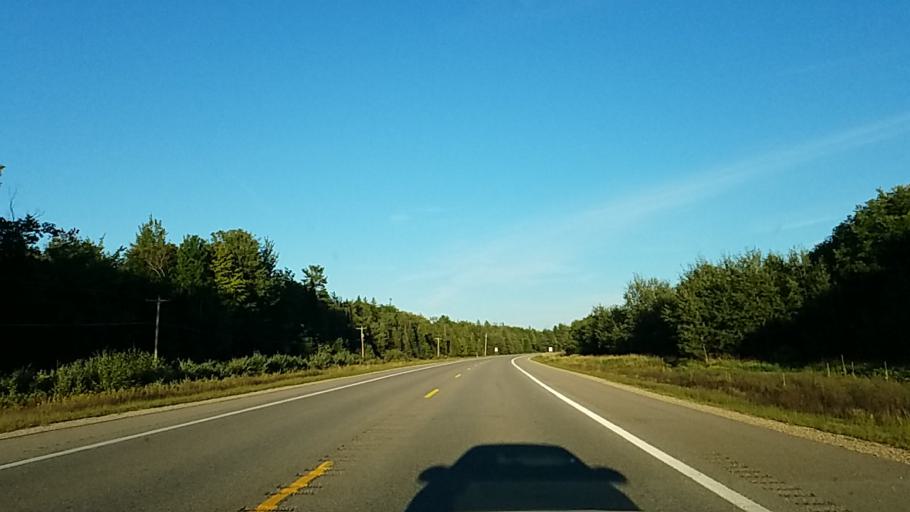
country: US
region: Michigan
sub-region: Alger County
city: Munising
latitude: 46.4424
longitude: -86.7351
